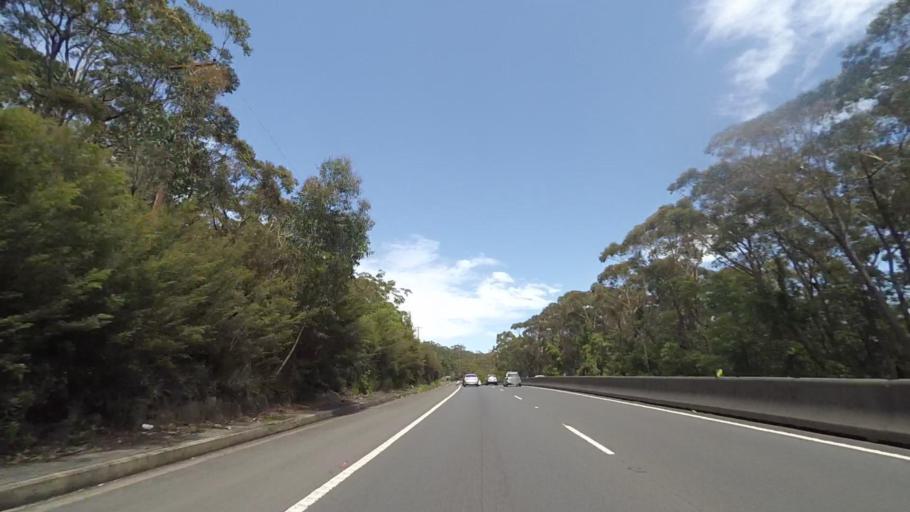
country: AU
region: New South Wales
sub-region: Wollongong
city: Bulli
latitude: -34.3185
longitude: 150.8903
